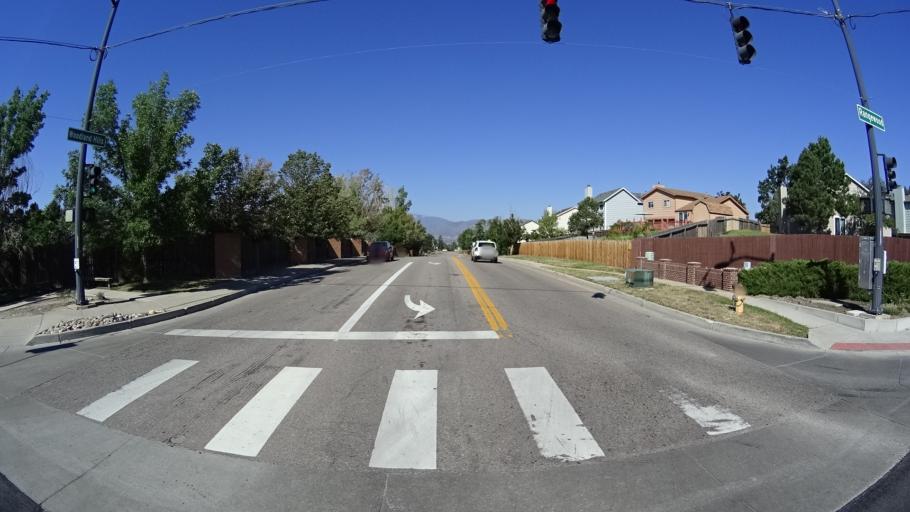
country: US
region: Colorado
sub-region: El Paso County
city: Cimarron Hills
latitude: 38.9327
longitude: -104.7541
